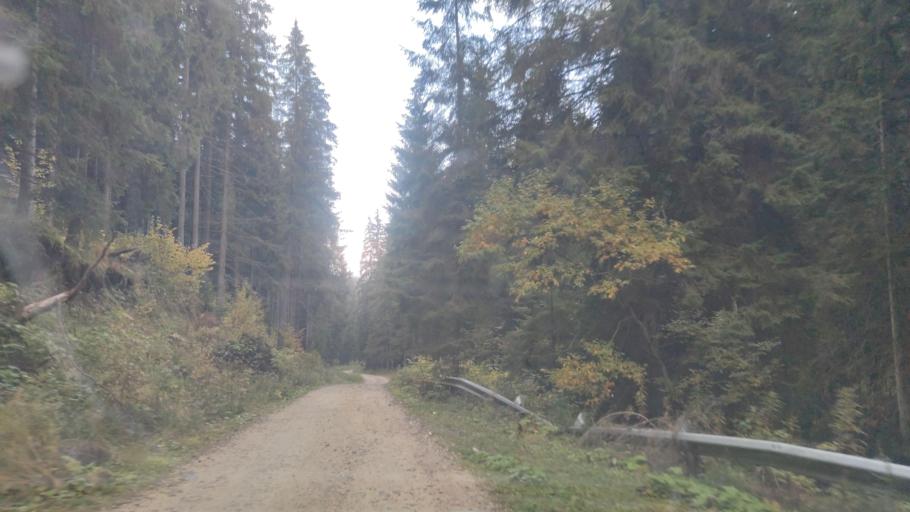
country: RO
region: Harghita
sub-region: Comuna Madaras
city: Madaras
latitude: 46.4750
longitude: 25.6478
